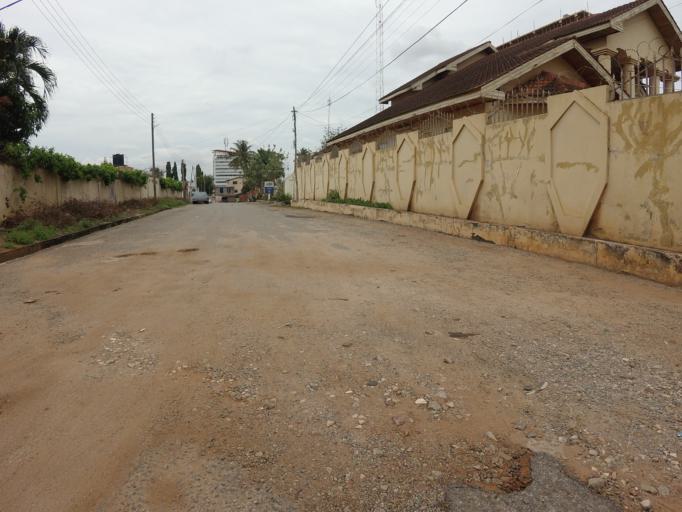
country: GH
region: Greater Accra
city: Accra
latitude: 5.5979
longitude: -0.2253
